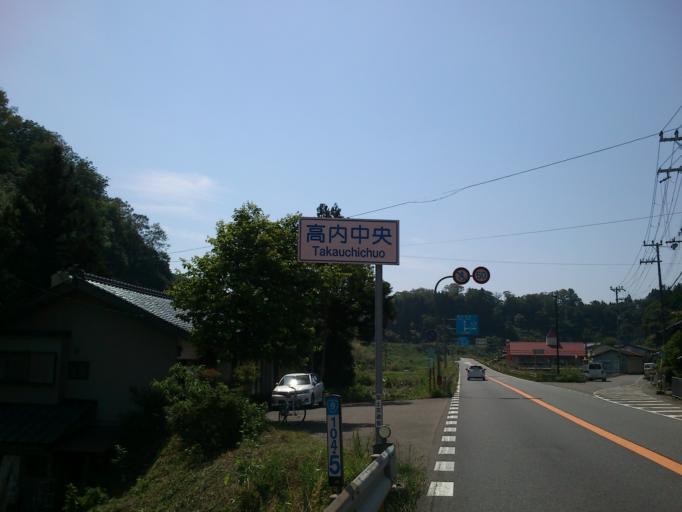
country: JP
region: Kyoto
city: Fukuchiyama
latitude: 35.3283
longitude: 134.9497
